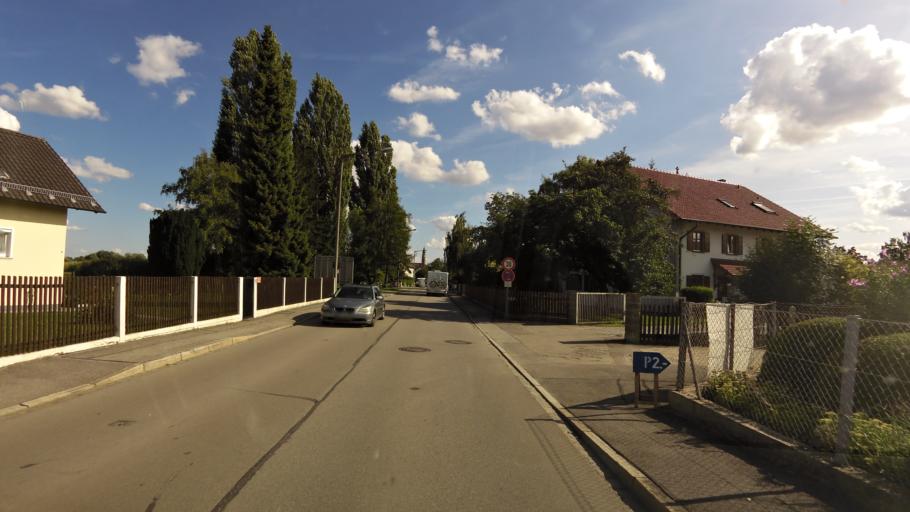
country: DE
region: Bavaria
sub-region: Lower Bavaria
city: Straubing
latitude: 48.8939
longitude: 12.5623
